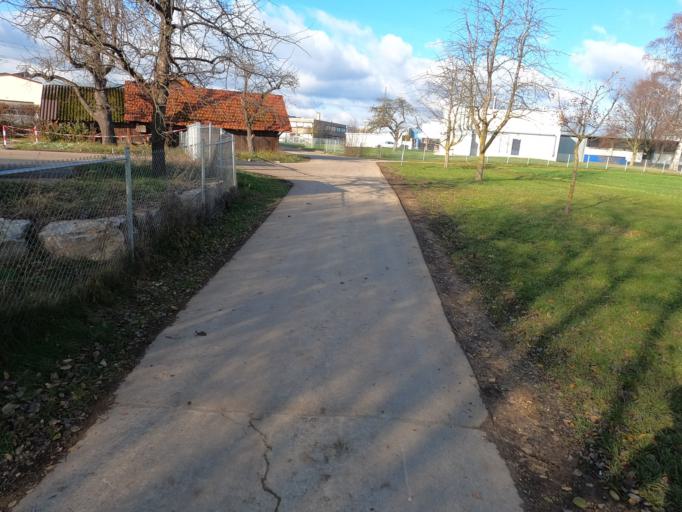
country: DE
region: Baden-Wuerttemberg
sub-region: Regierungsbezirk Stuttgart
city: Hattenhofen
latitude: 48.6633
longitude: 9.5553
